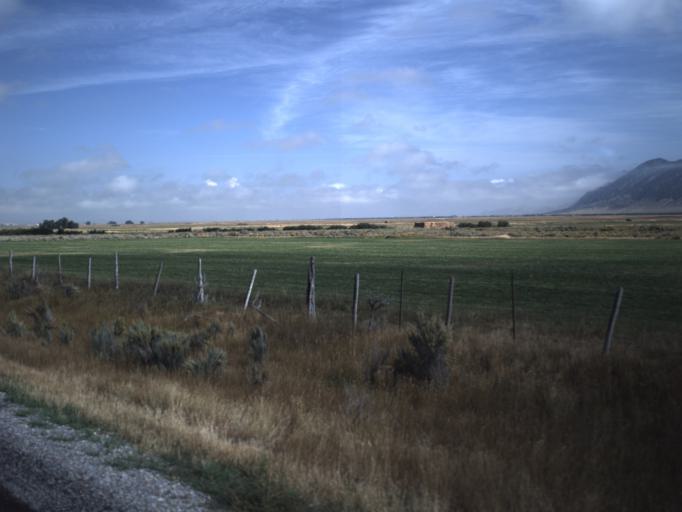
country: US
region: Utah
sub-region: Rich County
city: Randolph
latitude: 41.6005
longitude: -111.1754
